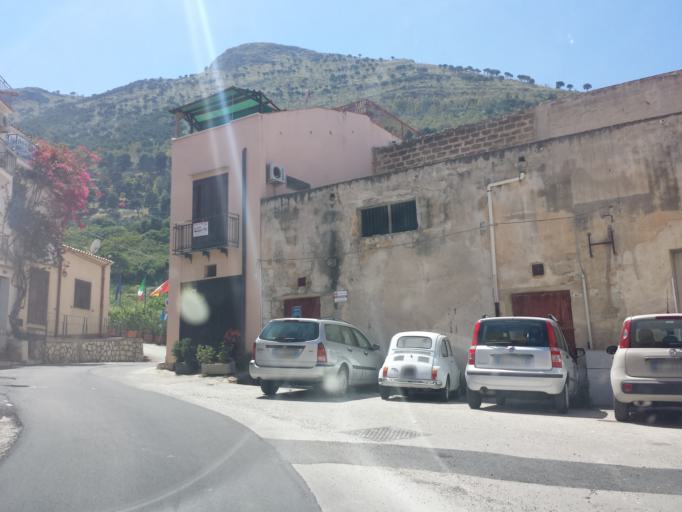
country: IT
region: Sicily
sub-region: Trapani
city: Castellammare del Golfo
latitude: 38.0280
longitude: 12.8795
